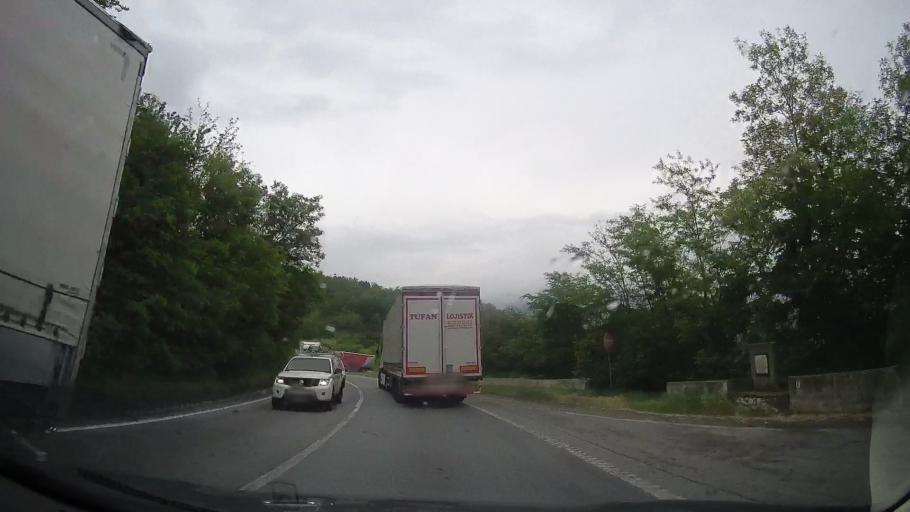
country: RO
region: Caras-Severin
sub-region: Comuna Mehadia
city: Plugova
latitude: 44.9712
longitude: 22.3477
